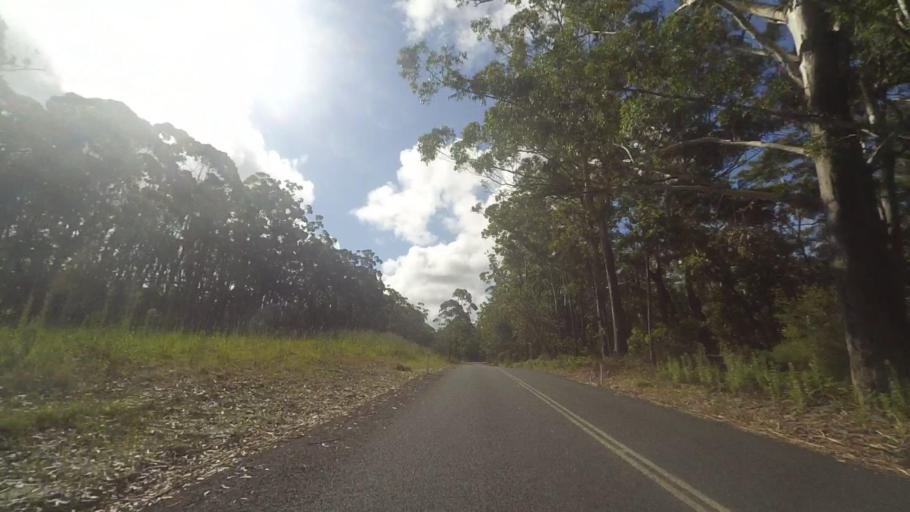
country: AU
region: New South Wales
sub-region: Great Lakes
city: Forster
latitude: -32.4229
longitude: 152.4956
